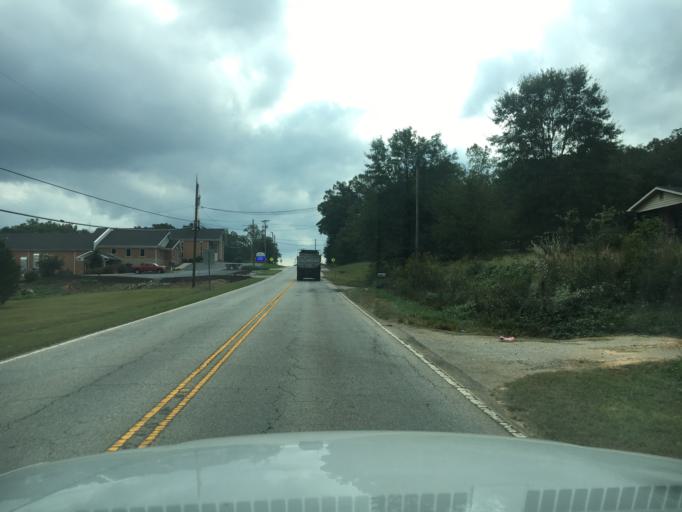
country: US
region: South Carolina
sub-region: Greenville County
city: Greer
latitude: 35.0005
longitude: -82.2518
